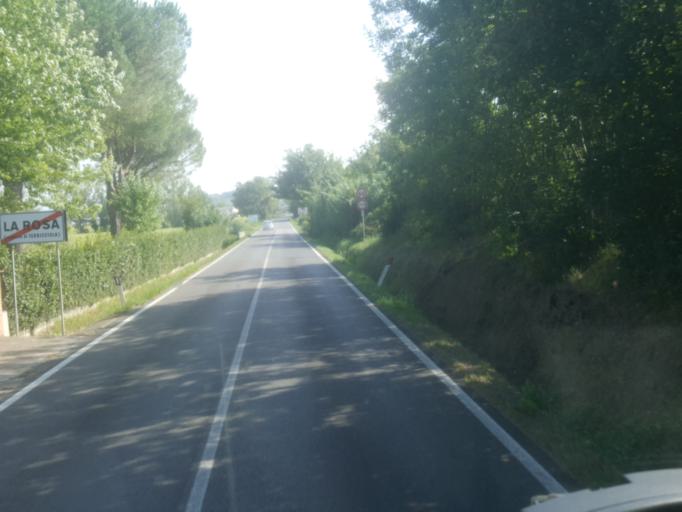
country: IT
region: Tuscany
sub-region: Province of Pisa
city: Peccioli
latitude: 43.5346
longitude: 10.7012
